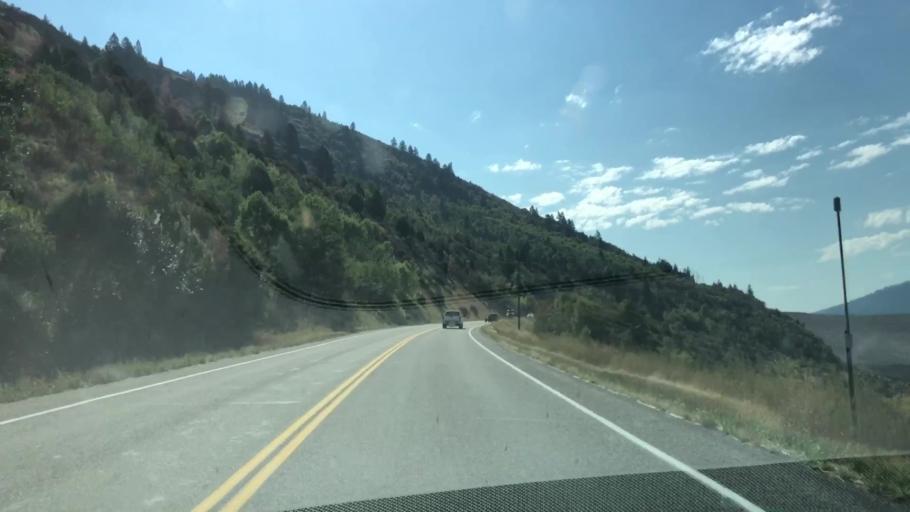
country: US
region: Idaho
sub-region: Teton County
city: Victor
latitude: 43.3428
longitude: -111.2034
